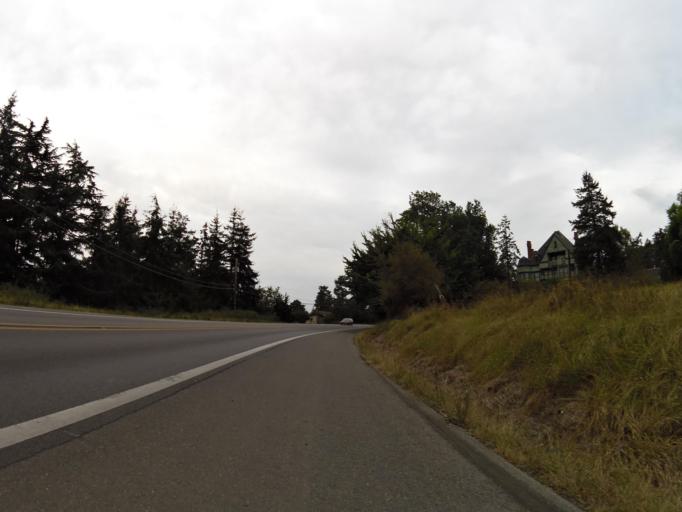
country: US
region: Washington
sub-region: Jefferson County
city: Port Townsend
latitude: 48.1041
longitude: -122.7863
